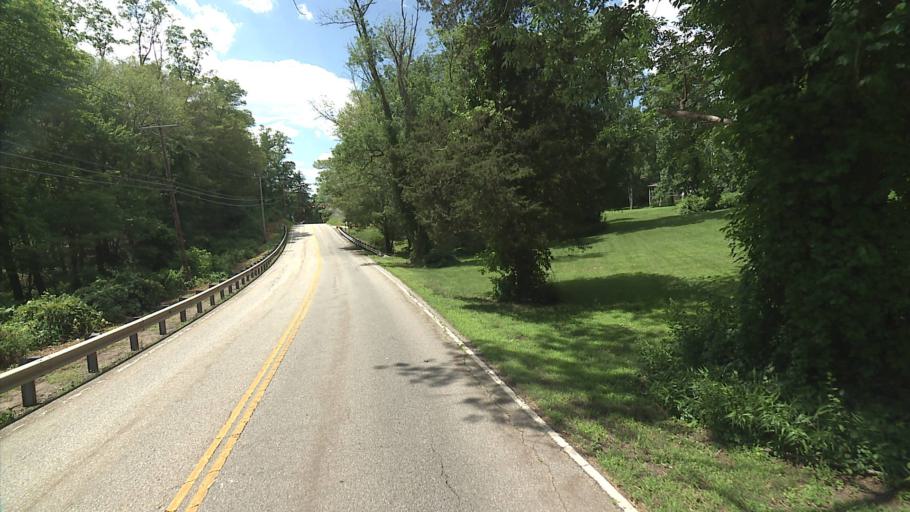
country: US
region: Connecticut
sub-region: Middlesex County
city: Higganum
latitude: 41.5295
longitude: -72.5352
